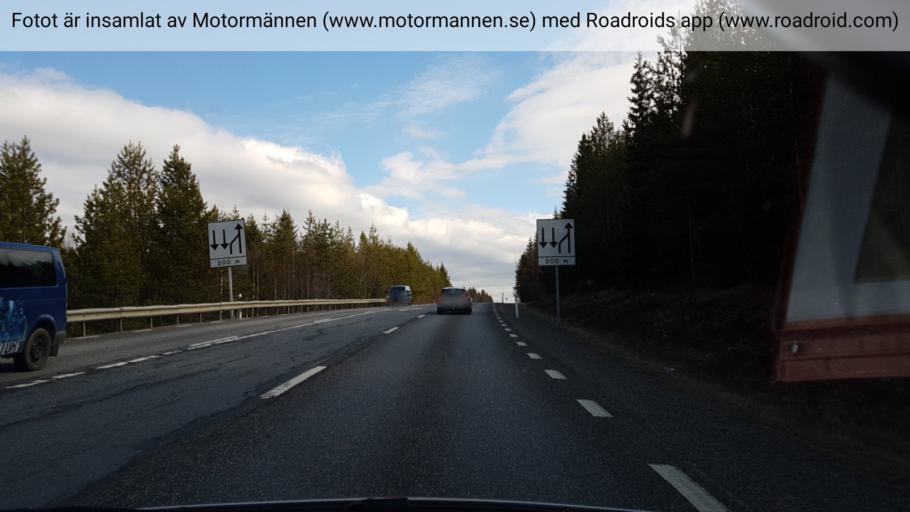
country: SE
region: Vaesternorrland
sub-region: Solleftea Kommun
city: Solleftea
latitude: 63.1253
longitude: 17.4842
